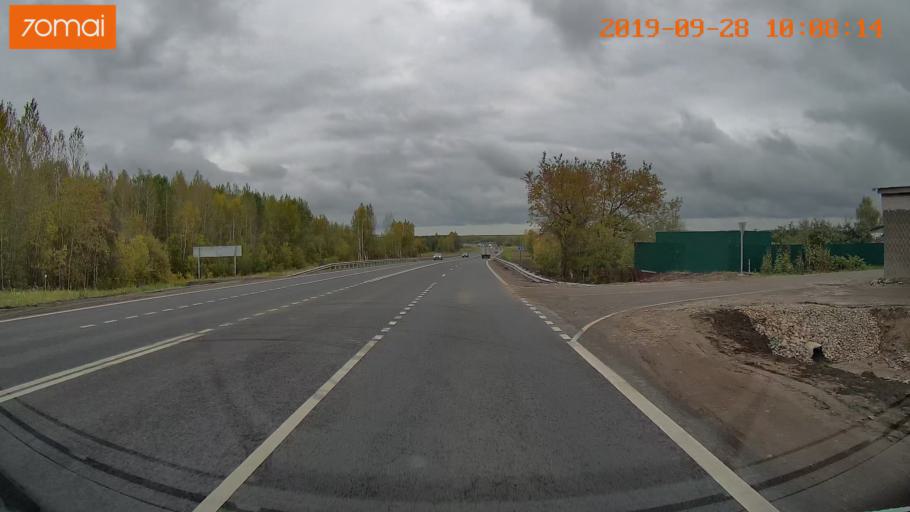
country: RU
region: Jaroslavl
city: Yaroslavl
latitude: 57.5549
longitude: 39.8752
